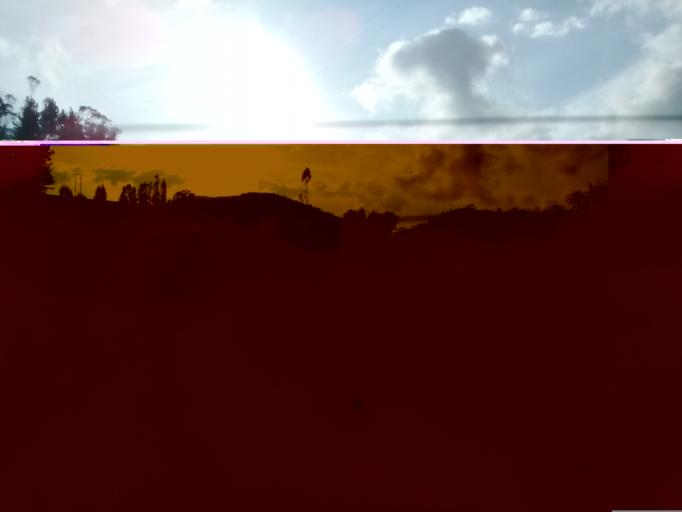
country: CO
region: Cundinamarca
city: Sibate
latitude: 4.4348
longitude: -74.2837
